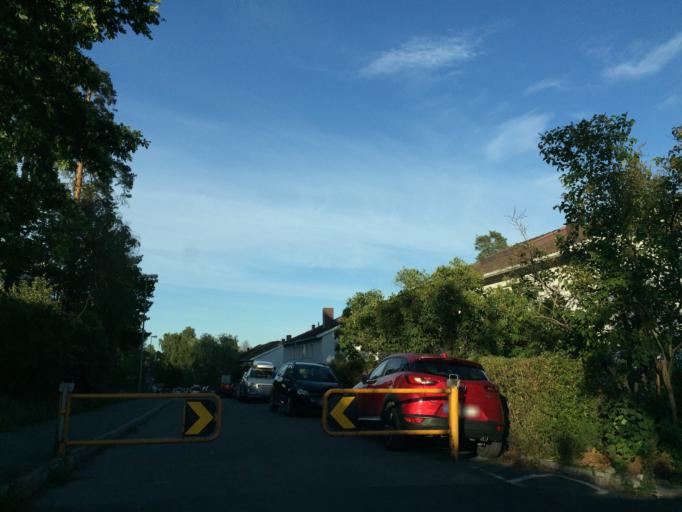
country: NO
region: Akershus
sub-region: Baerum
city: Lysaker
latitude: 59.9040
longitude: 10.6097
